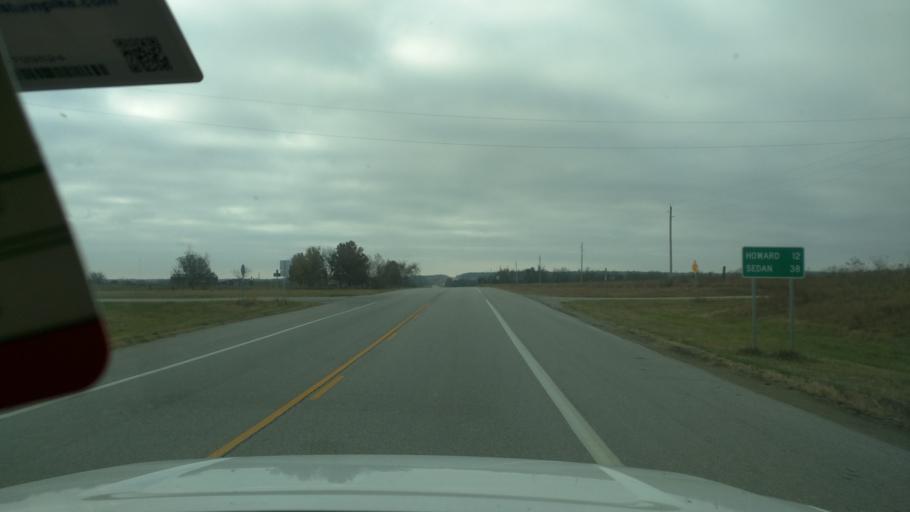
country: US
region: Kansas
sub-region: Elk County
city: Howard
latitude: 37.6358
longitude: -96.2532
